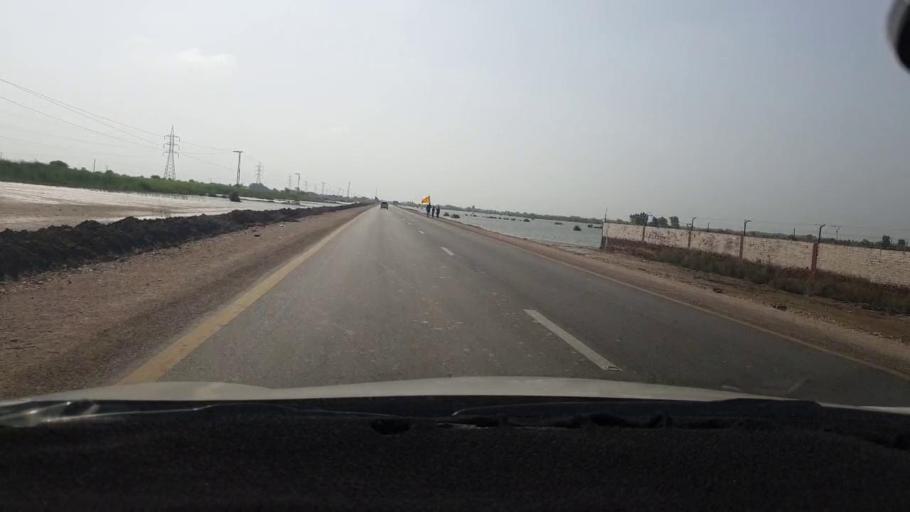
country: PK
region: Sindh
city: Jhol
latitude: 25.8986
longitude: 69.0240
